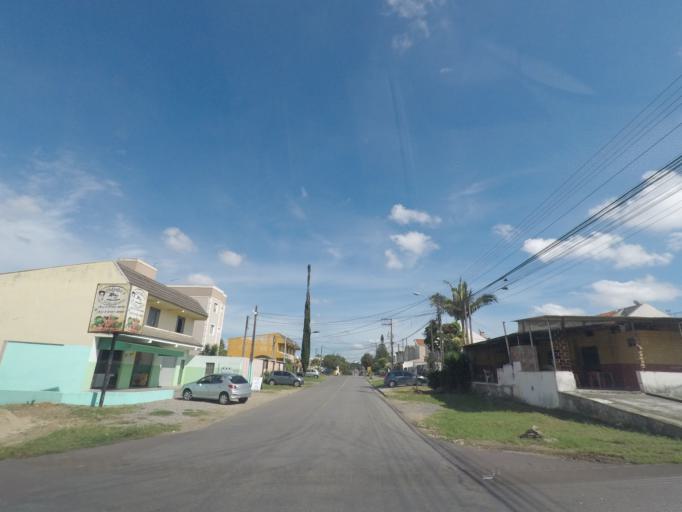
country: BR
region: Parana
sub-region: Curitiba
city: Curitiba
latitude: -25.4788
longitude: -49.2740
